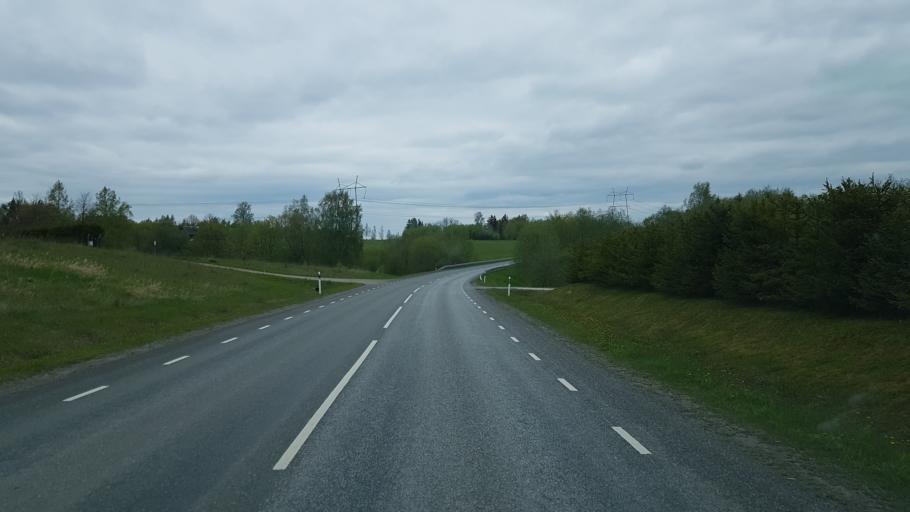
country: EE
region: Viljandimaa
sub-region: Viljandi linn
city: Viljandi
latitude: 58.3829
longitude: 25.6055
